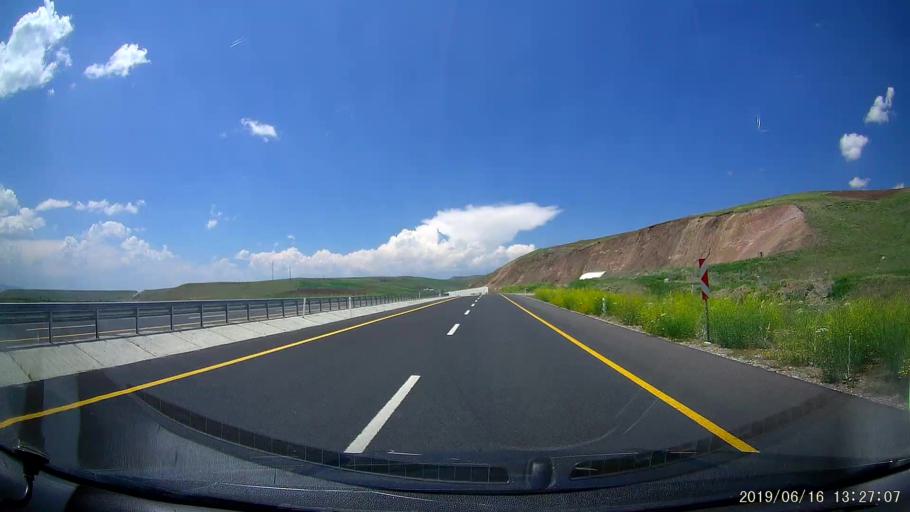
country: TR
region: Agri
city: Taslicay
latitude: 39.6671
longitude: 43.3157
